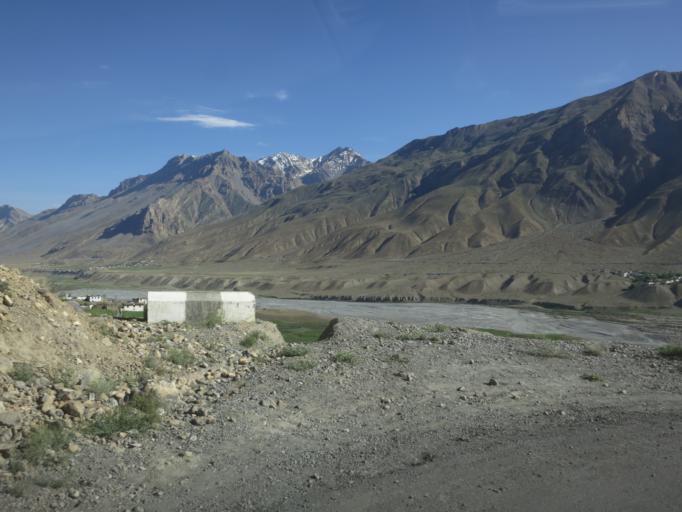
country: IN
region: Himachal Pradesh
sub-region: Shimla
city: Sarahan
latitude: 32.2961
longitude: 78.0100
